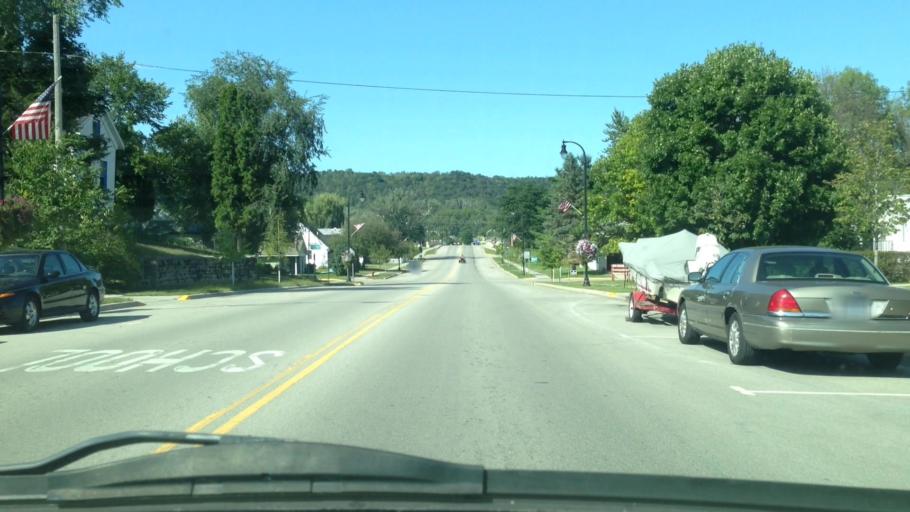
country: US
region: Minnesota
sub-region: Fillmore County
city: Rushford
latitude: 43.8120
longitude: -91.7532
